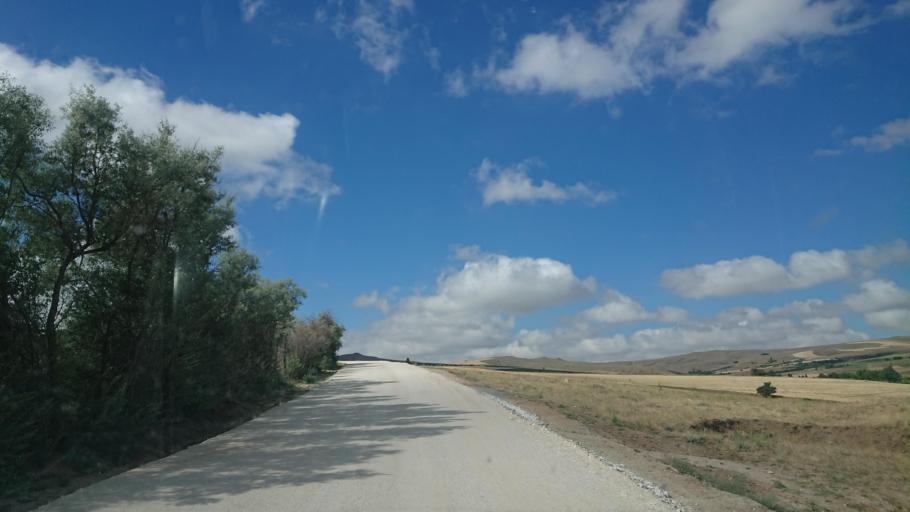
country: TR
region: Aksaray
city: Agacoren
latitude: 38.8548
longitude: 33.9406
